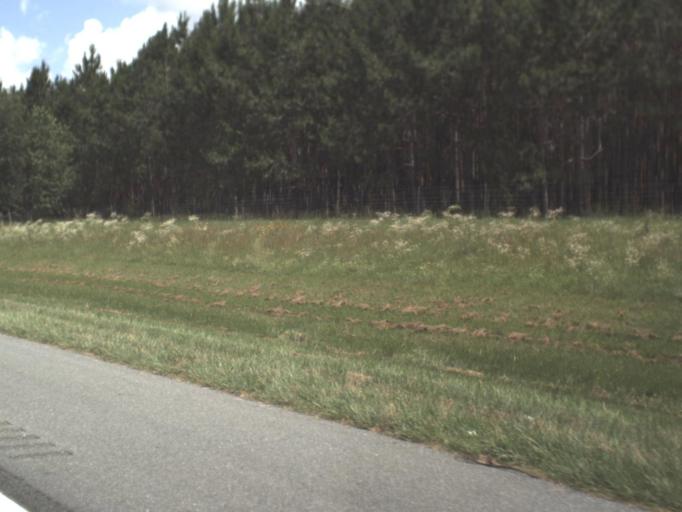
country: US
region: Florida
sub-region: Suwannee County
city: Wellborn
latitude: 30.2896
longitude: -82.7751
